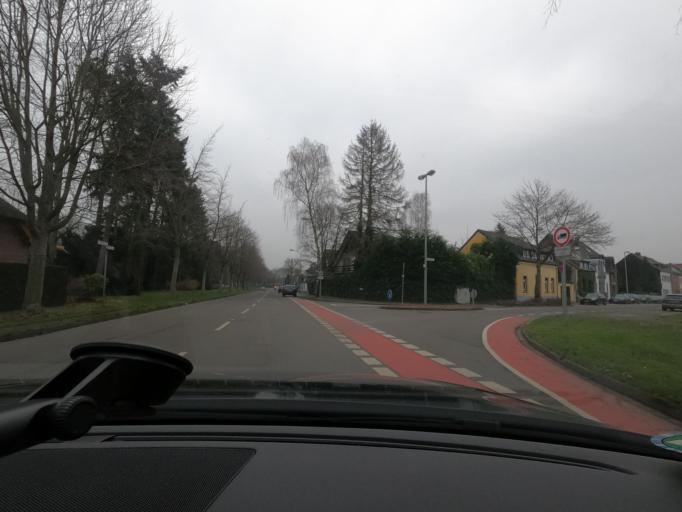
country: DE
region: North Rhine-Westphalia
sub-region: Regierungsbezirk Dusseldorf
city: Krefeld
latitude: 51.3511
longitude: 6.5937
